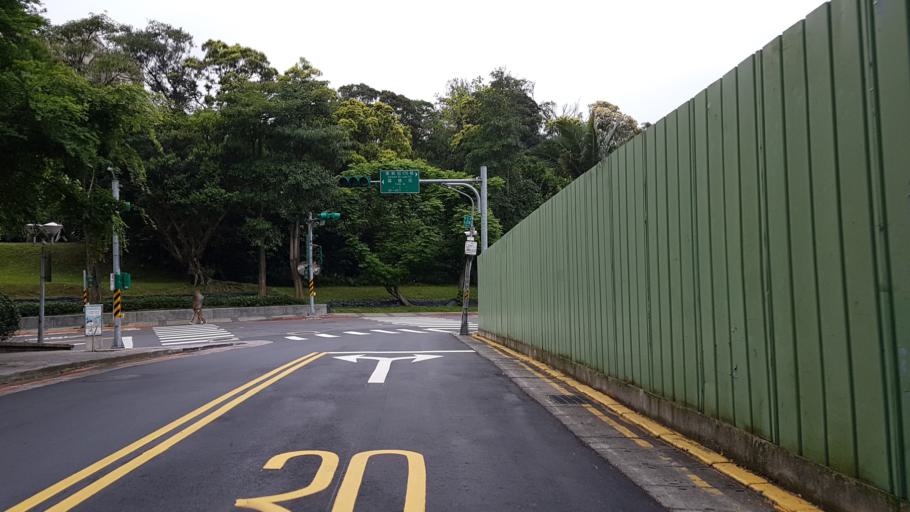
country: TW
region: Taipei
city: Taipei
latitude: 25.0402
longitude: 121.5932
